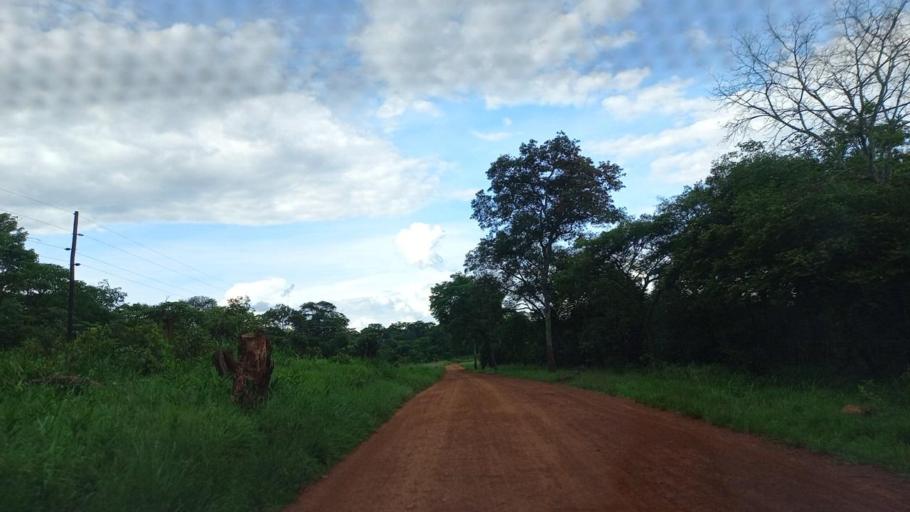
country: ZM
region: North-Western
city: Mwinilunga
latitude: -11.7845
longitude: 24.3735
